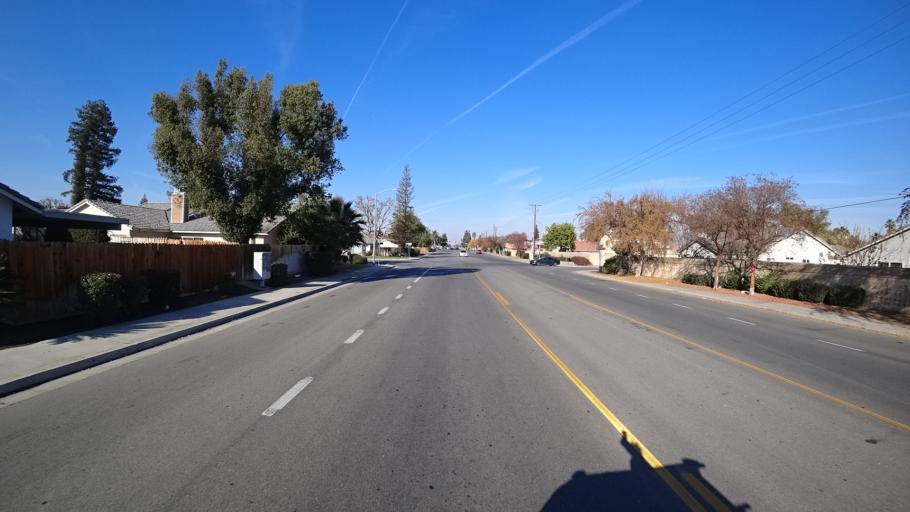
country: US
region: California
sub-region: Kern County
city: Greenfield
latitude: 35.2933
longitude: -119.0479
